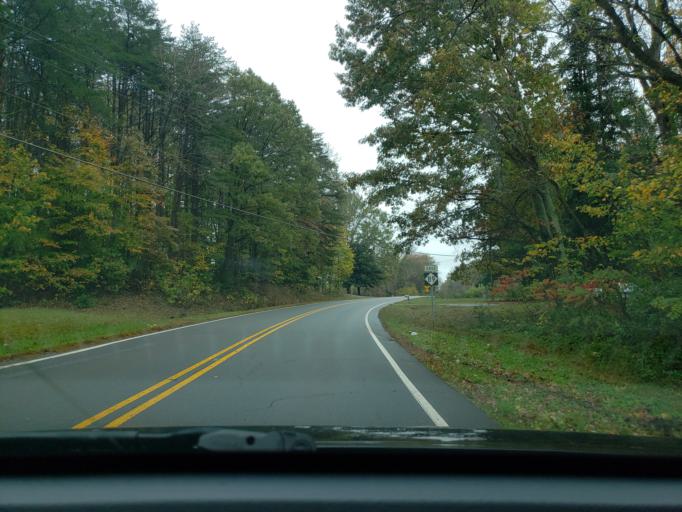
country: US
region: North Carolina
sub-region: Stokes County
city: Walnut Cove
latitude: 36.3513
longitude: -80.1549
